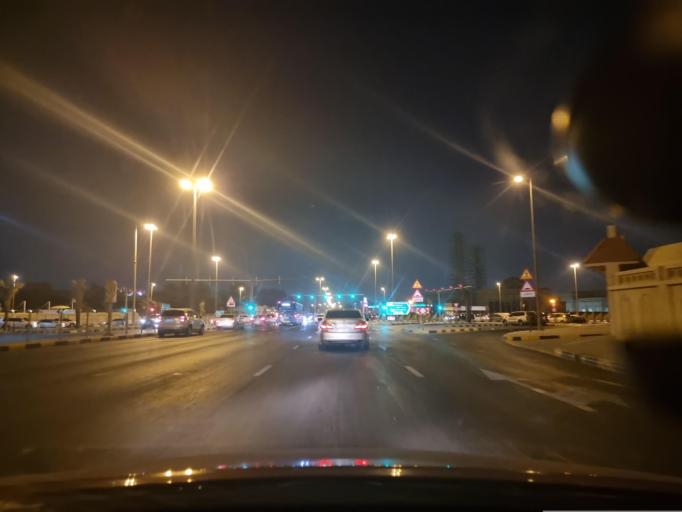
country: AE
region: Ash Shariqah
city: Sharjah
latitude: 25.3656
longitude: 55.4339
